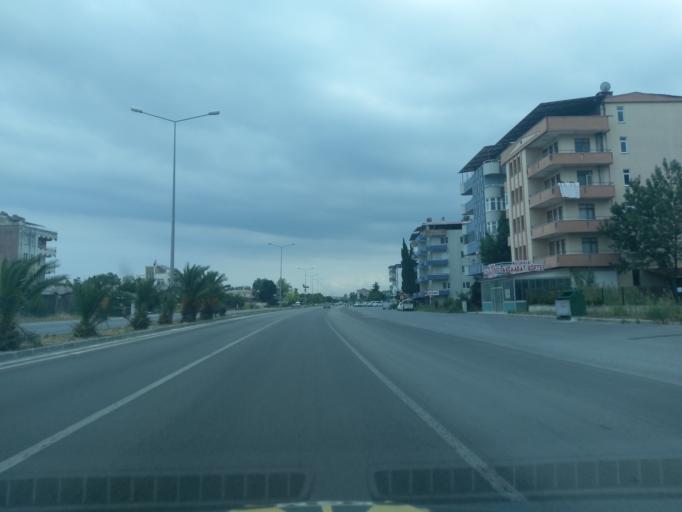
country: TR
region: Samsun
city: Taflan
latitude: 41.4005
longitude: 36.1915
